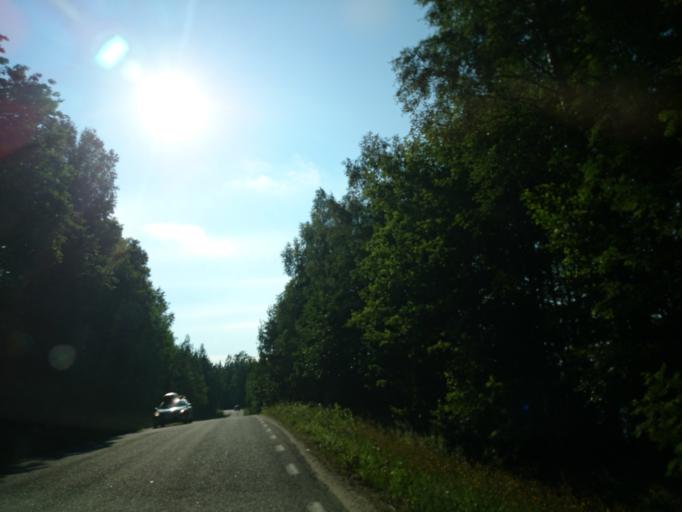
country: SE
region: Vaesternorrland
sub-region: Sundsvalls Kommun
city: Njurundabommen
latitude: 62.2210
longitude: 17.3181
